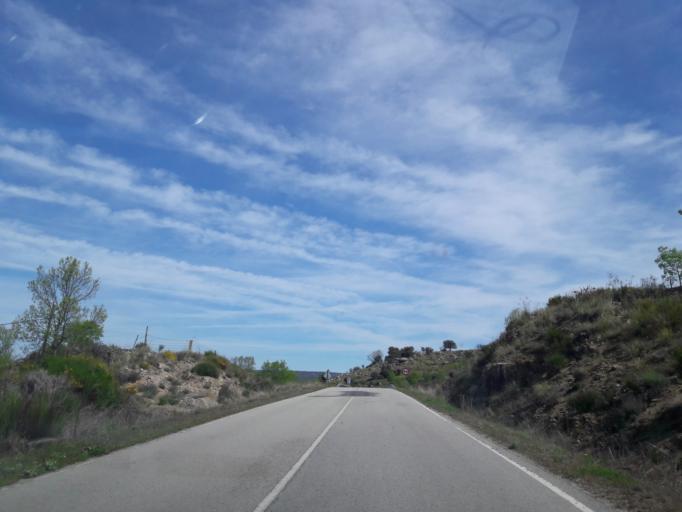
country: ES
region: Castille and Leon
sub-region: Provincia de Salamanca
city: Sanchotello
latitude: 40.4446
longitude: -5.7360
